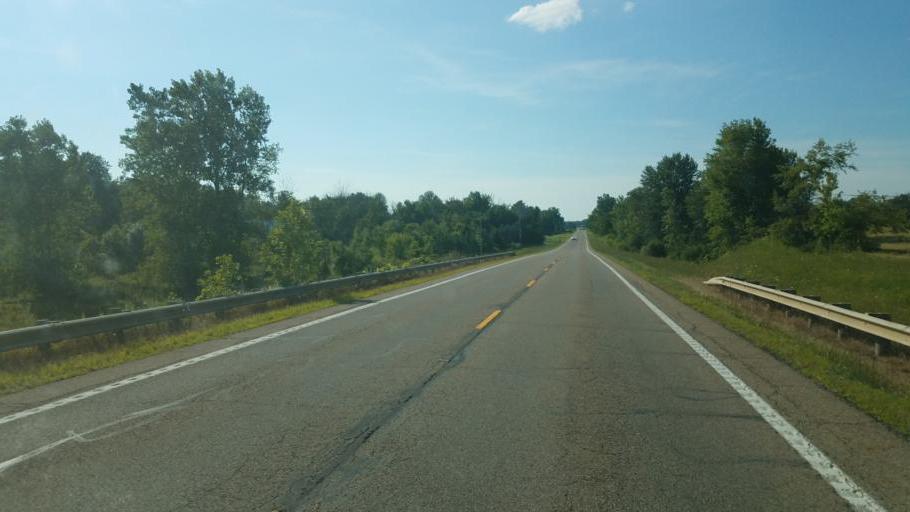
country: US
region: Ohio
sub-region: Morrow County
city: Mount Gilead
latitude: 40.5198
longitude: -82.7495
